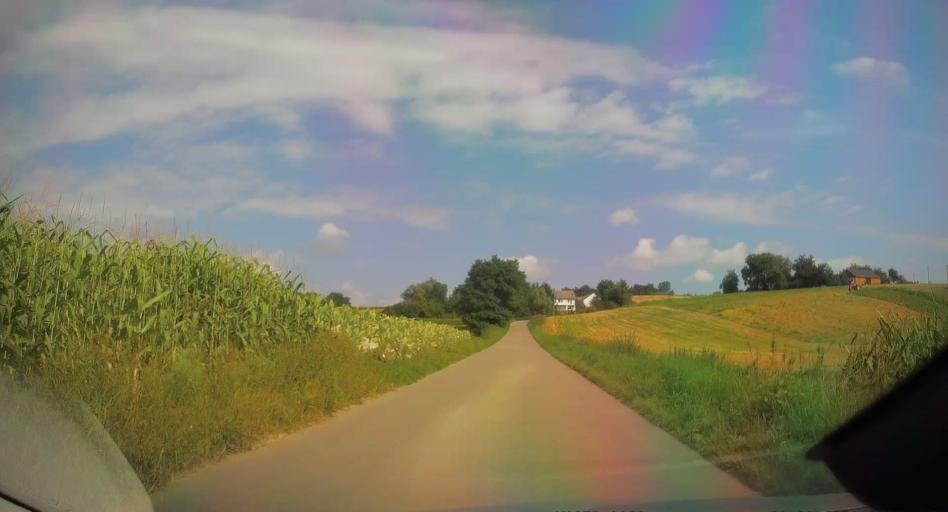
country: PL
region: Lesser Poland Voivodeship
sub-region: Powiat proszowicki
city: Nowe Brzesko
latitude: 50.1533
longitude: 20.4411
